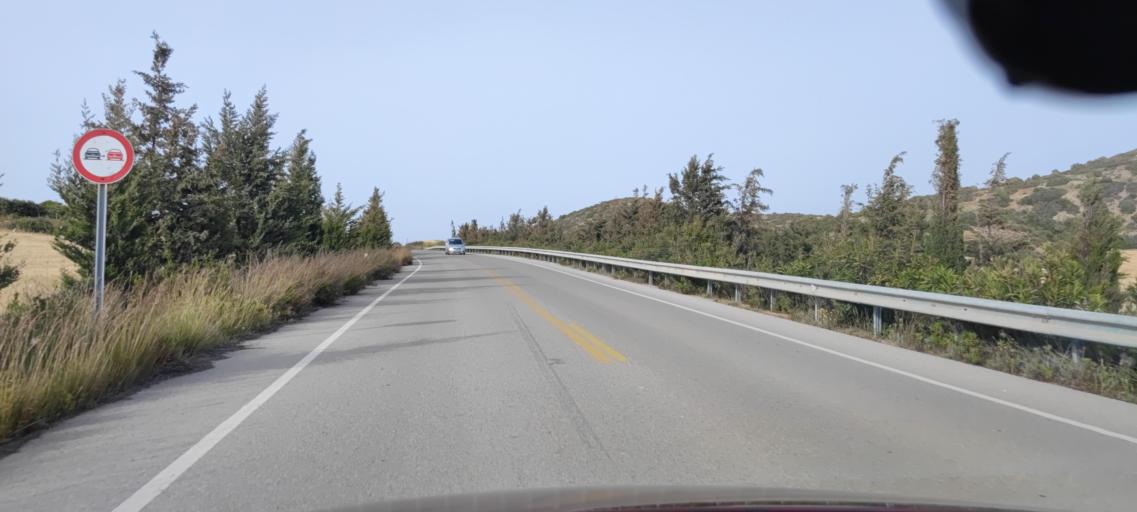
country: CY
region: Ammochostos
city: Leonarisso
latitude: 35.4881
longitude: 34.0783
